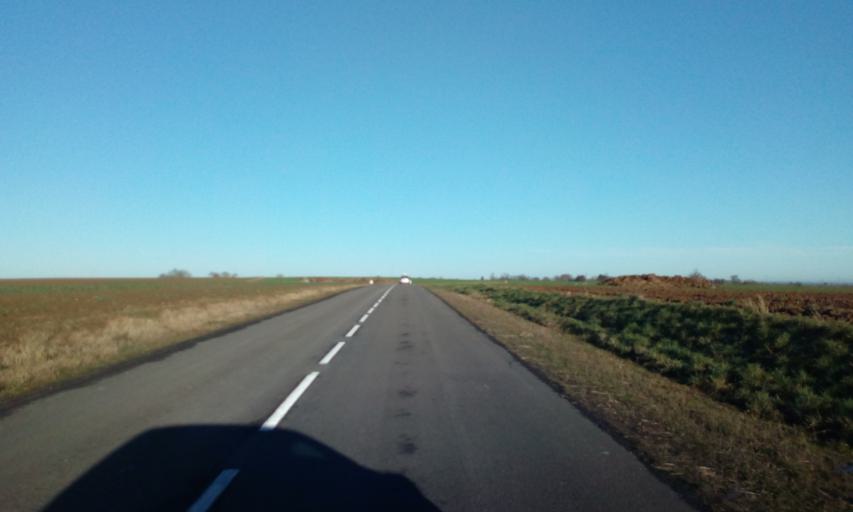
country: FR
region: Picardie
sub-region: Departement de l'Aisne
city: Rozoy-sur-Serre
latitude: 49.7023
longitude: 4.1995
